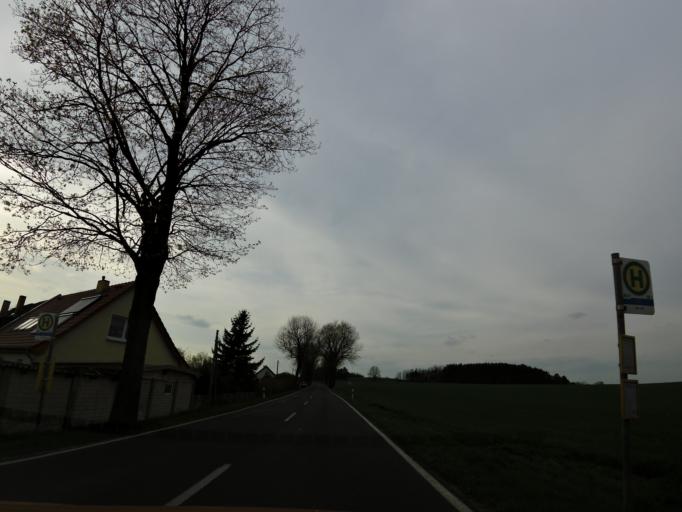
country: DE
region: Brandenburg
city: Mittenwalde
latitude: 52.2531
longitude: 13.5546
